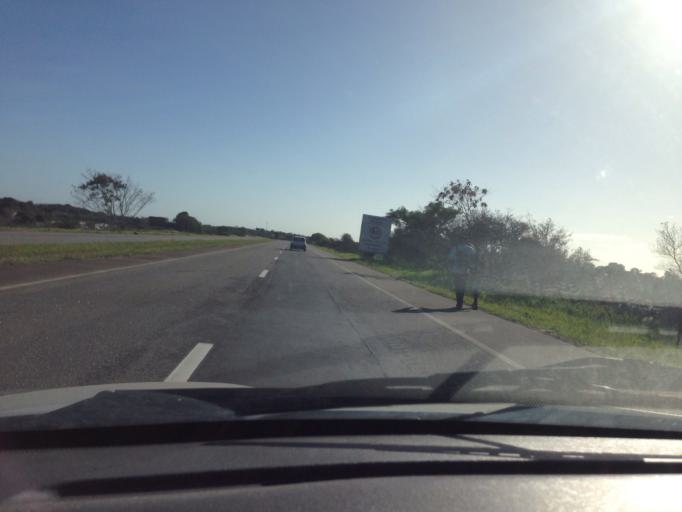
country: BR
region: Espirito Santo
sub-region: Guarapari
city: Guarapari
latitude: -20.6132
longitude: -40.4295
